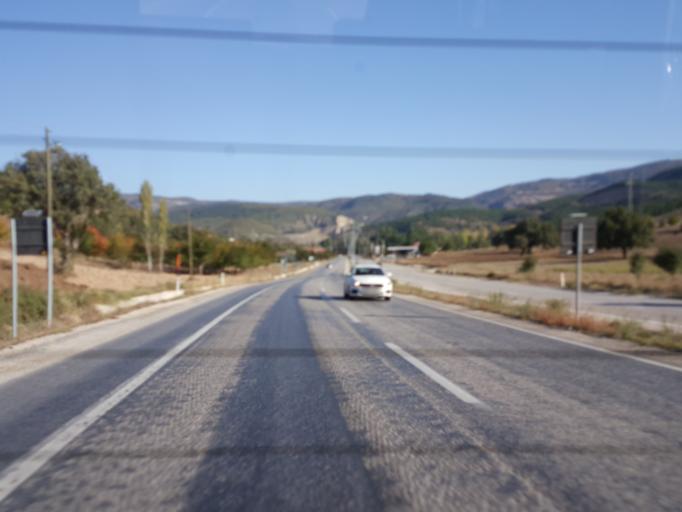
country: TR
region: Amasya
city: Ezinepazari
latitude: 40.5599
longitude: 36.1383
